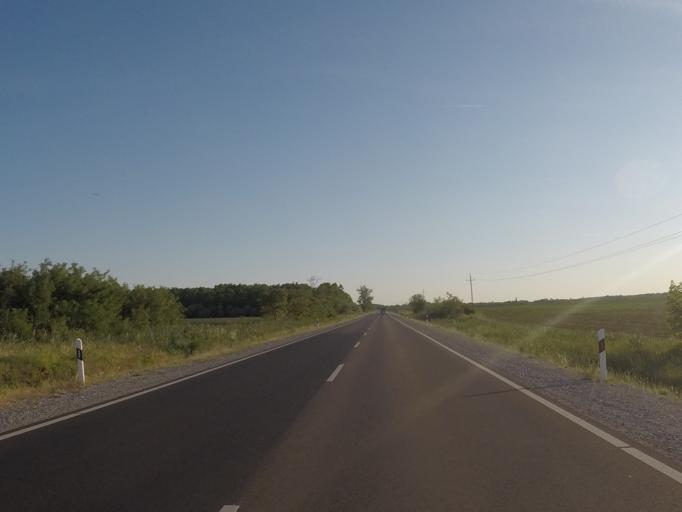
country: HU
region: Heves
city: Erdotelek
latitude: 47.6687
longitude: 20.3620
